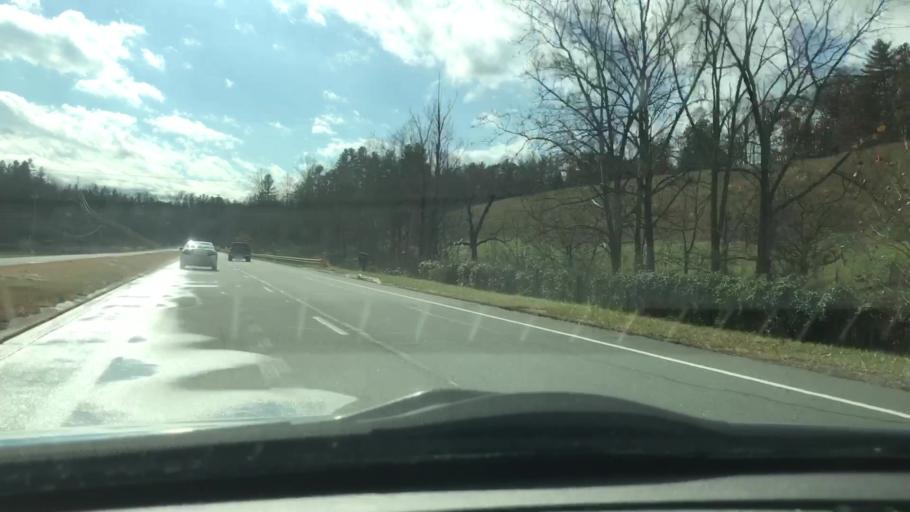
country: US
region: North Carolina
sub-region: Madison County
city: Mars Hill
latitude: 35.8603
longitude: -82.4862
